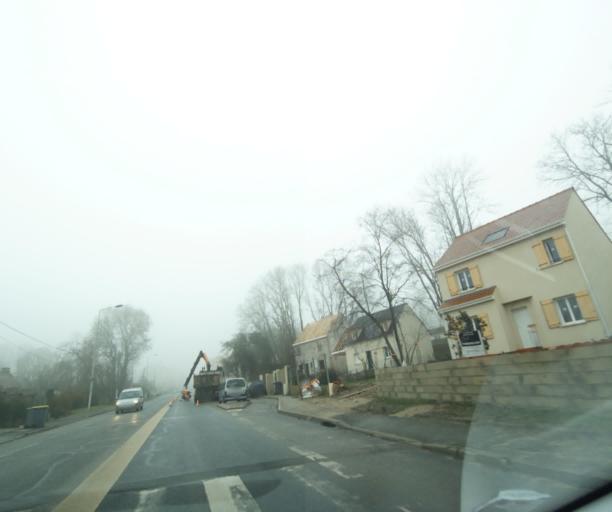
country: FR
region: Ile-de-France
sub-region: Departement de Seine-et-Marne
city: Dammartin-en-Goele
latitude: 49.0554
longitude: 2.6956
